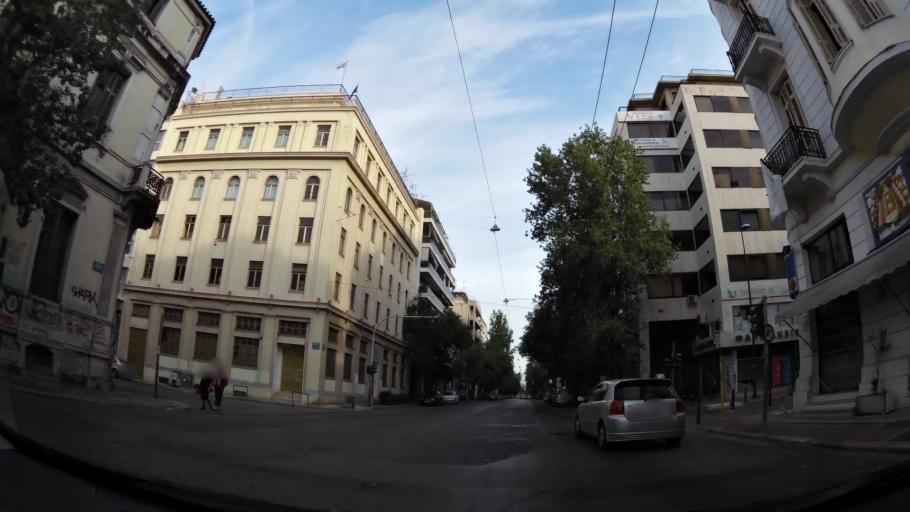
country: GR
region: Attica
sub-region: Nomarchia Athinas
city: Athens
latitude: 37.9891
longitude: 23.7268
